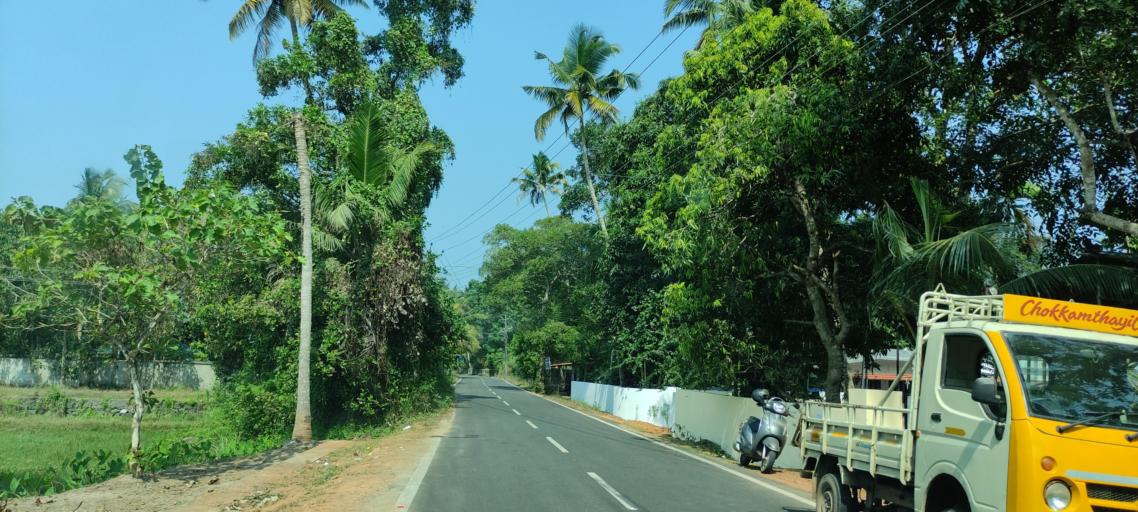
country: IN
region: Kerala
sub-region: Alappuzha
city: Shertallai
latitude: 9.5968
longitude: 76.3116
